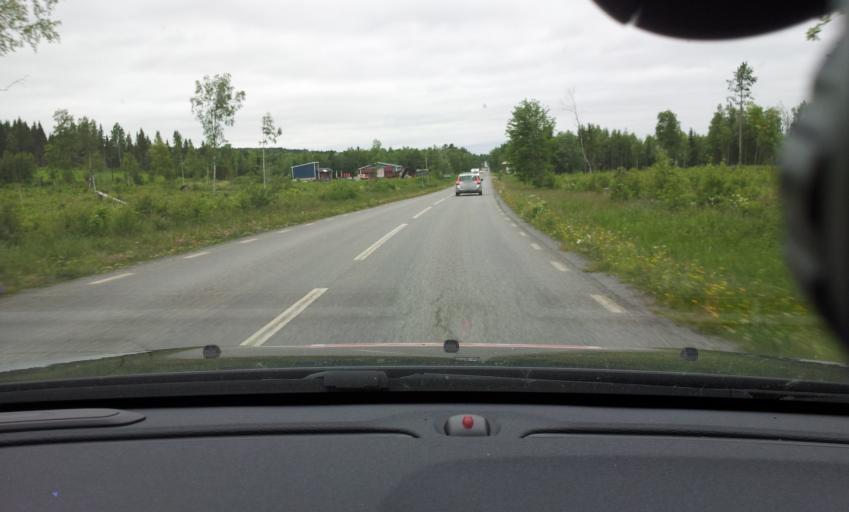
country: SE
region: Jaemtland
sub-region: Krokoms Kommun
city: Krokom
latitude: 63.1680
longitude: 14.1100
